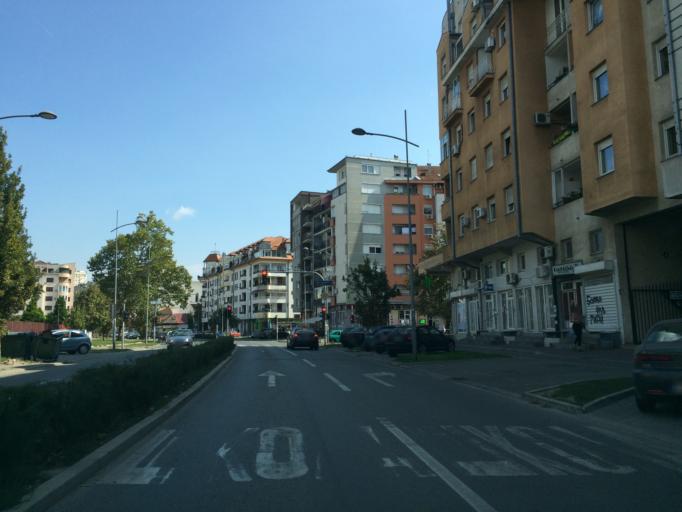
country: RS
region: Autonomna Pokrajina Vojvodina
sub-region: Juznobacki Okrug
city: Novi Sad
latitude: 45.2484
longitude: 19.8340
